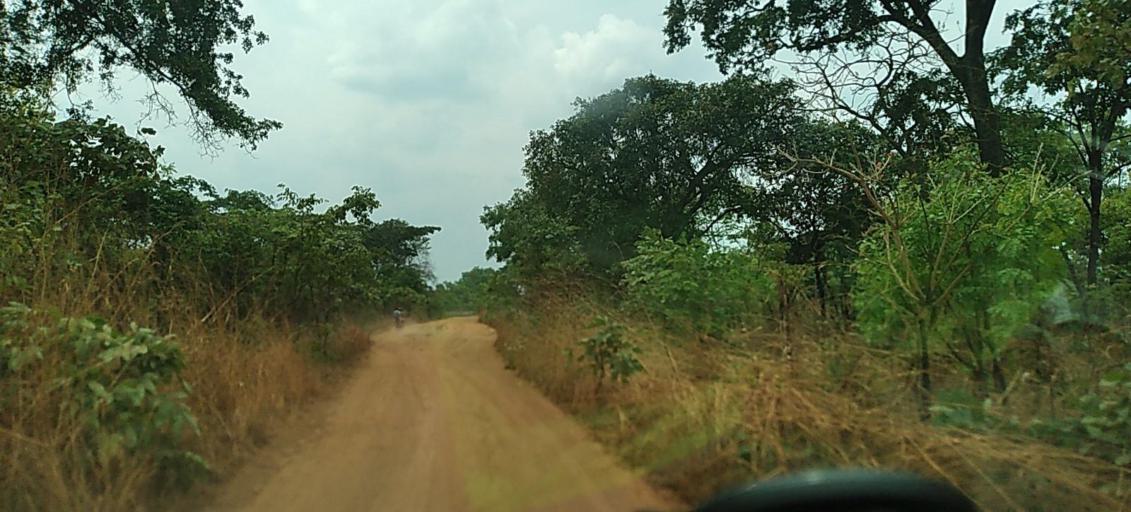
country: ZM
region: North-Western
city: Kansanshi
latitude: -12.0715
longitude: 26.3544
